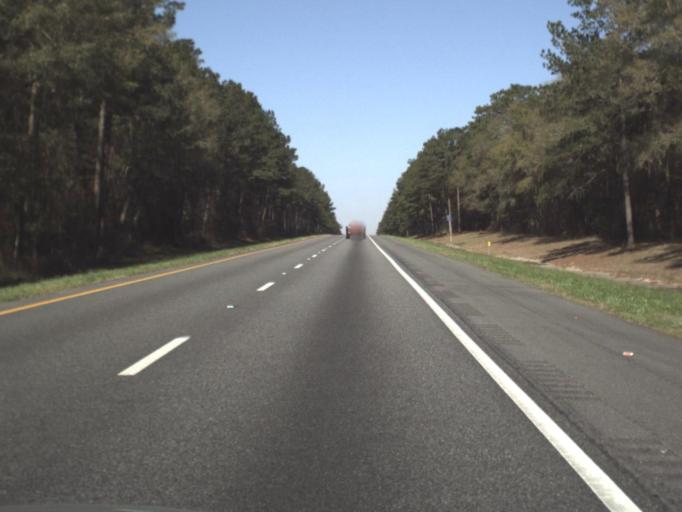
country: US
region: Florida
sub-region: Gadsden County
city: Midway
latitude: 30.5203
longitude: -84.4865
